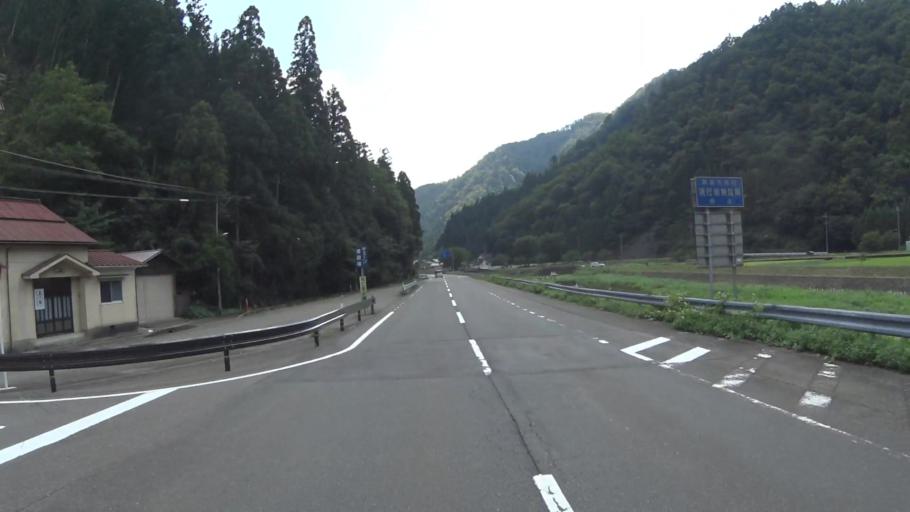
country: JP
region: Fukui
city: Obama
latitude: 35.3330
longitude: 135.5685
